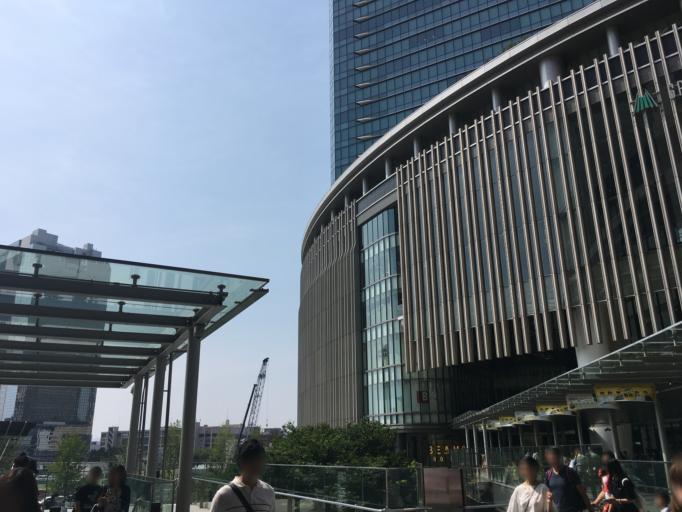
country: JP
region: Osaka
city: Osaka-shi
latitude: 34.7036
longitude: 135.4949
